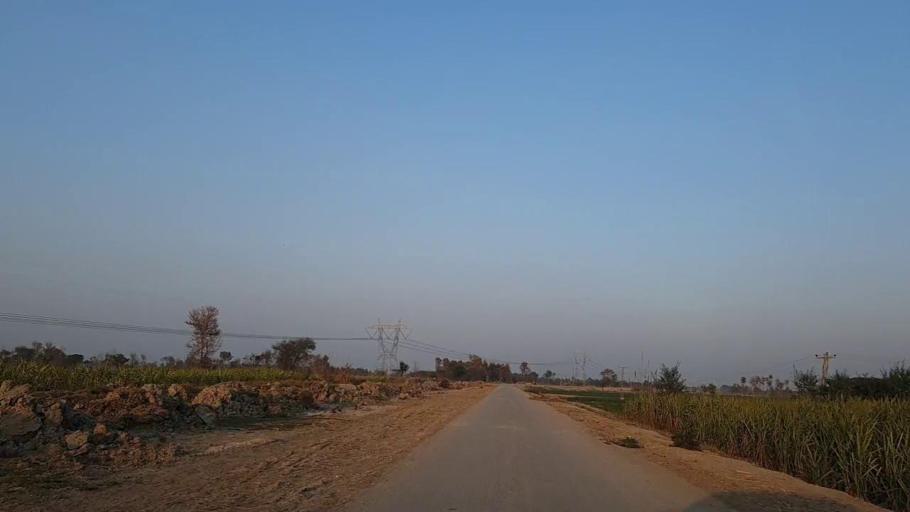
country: PK
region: Sindh
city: Moro
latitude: 26.7647
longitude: 68.0443
